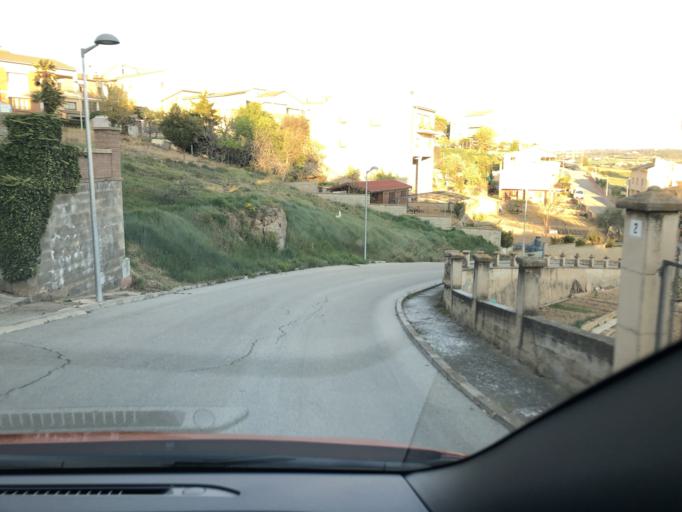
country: ES
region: Catalonia
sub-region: Provincia de Lleida
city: Solsona
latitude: 41.9872
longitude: 1.5155
